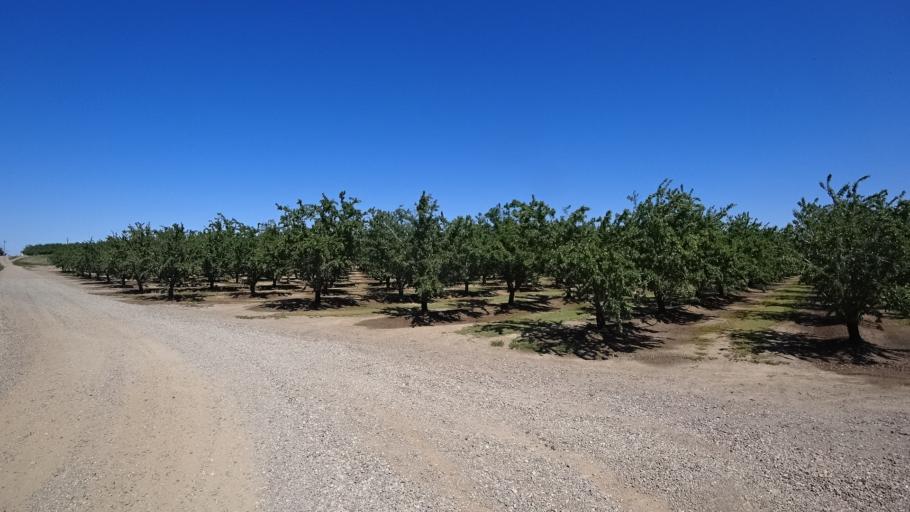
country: US
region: California
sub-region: Glenn County
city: Hamilton City
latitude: 39.7288
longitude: -122.0886
